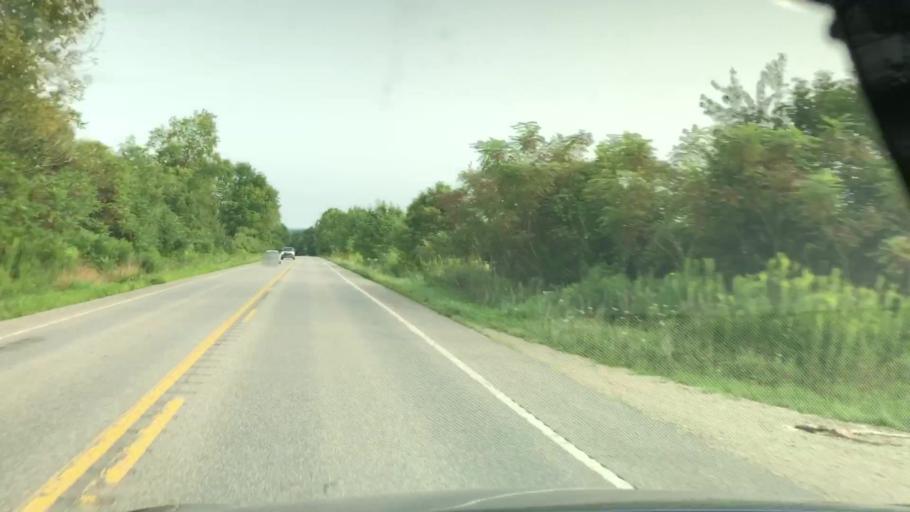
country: US
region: Pennsylvania
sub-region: Erie County
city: Union City
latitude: 41.8426
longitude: -79.8219
